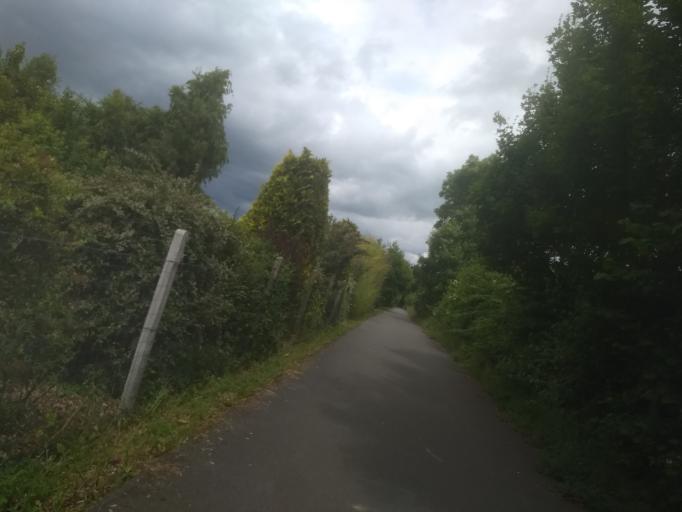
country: FR
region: Nord-Pas-de-Calais
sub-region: Departement du Pas-de-Calais
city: Beaumetz-les-Loges
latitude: 50.2398
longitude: 2.6628
